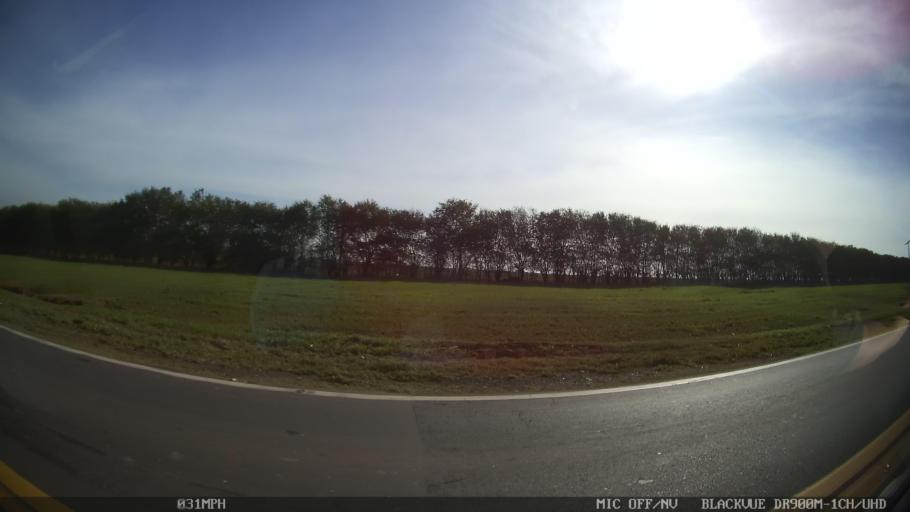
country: BR
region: Sao Paulo
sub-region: Rio Das Pedras
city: Rio das Pedras
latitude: -22.7969
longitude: -47.6059
